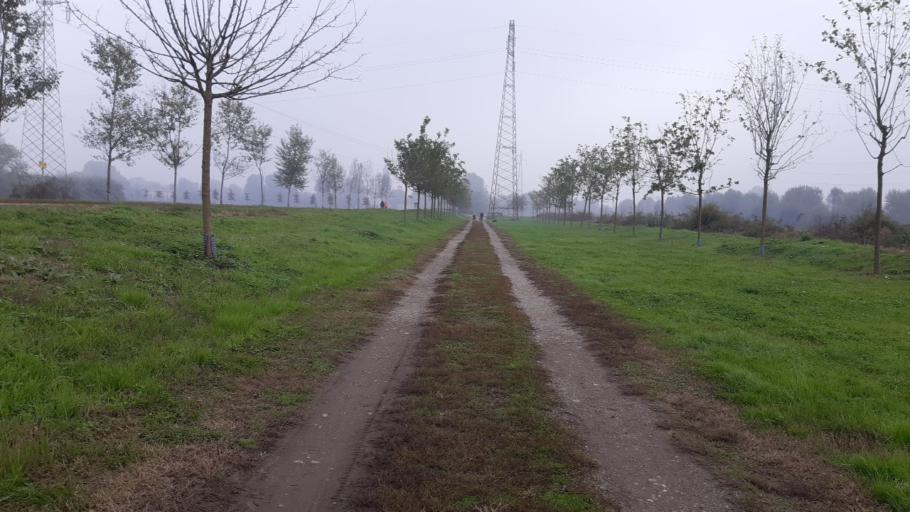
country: IT
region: Lombardy
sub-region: Citta metropolitana di Milano
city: Chiaravalle
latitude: 45.4184
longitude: 9.2282
